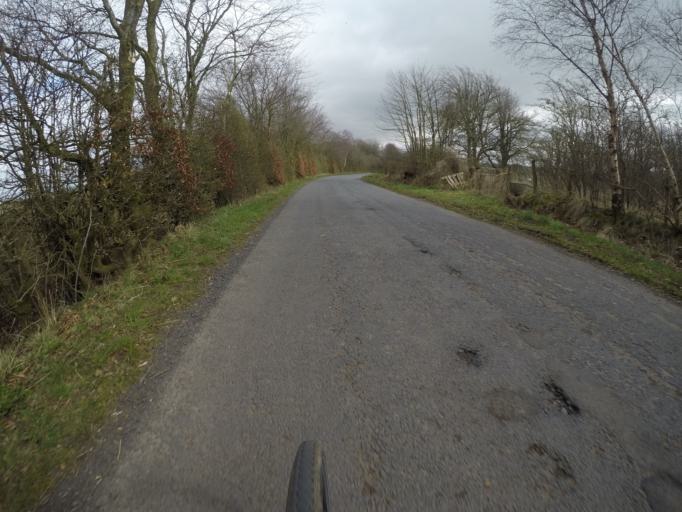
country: GB
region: Scotland
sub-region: North Ayrshire
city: Springside
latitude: 55.6701
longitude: -4.5770
